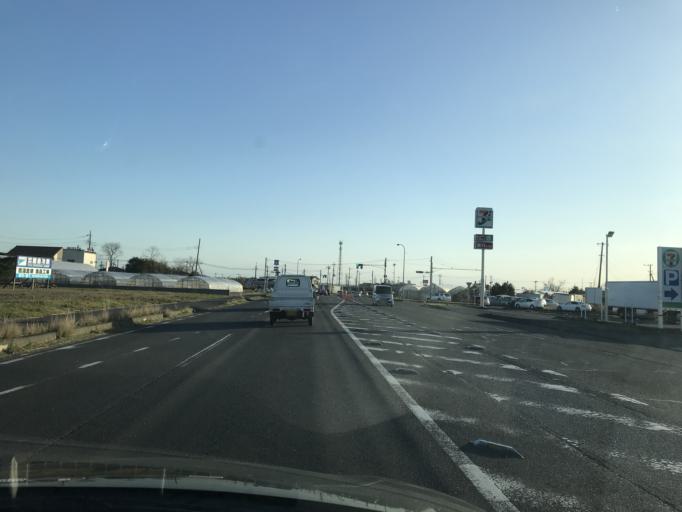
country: JP
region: Chiba
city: Omigawa
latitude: 35.8809
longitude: 140.6308
